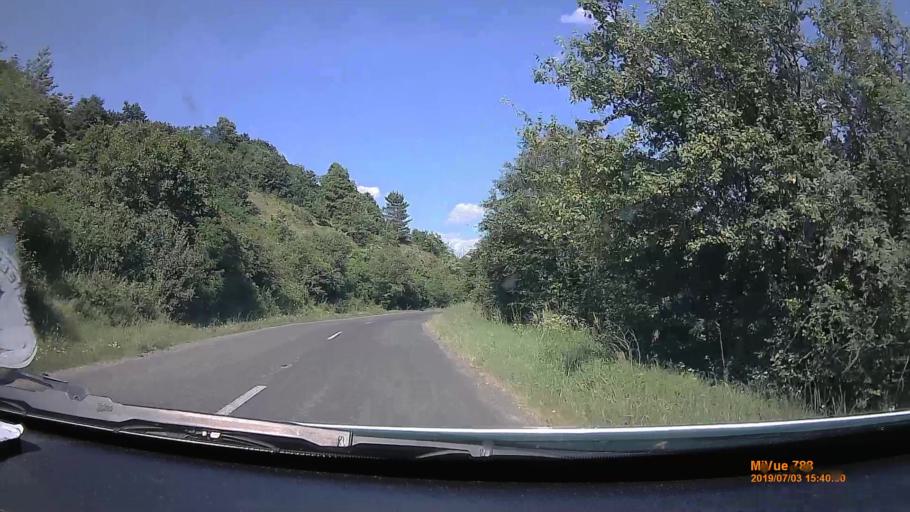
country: HU
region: Heves
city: Szilvasvarad
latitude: 48.1659
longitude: 20.4121
